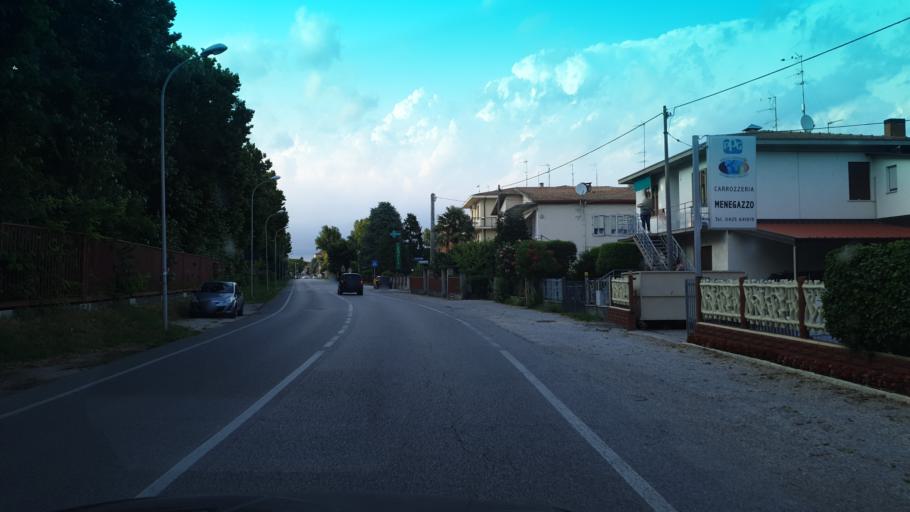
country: IT
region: Veneto
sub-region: Provincia di Rovigo
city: Lendinara
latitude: 45.0771
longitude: 11.5968
